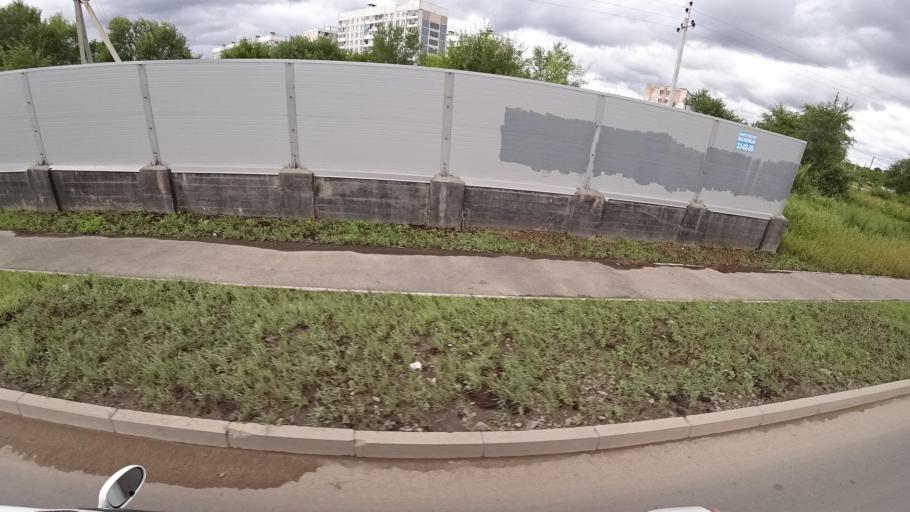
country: RU
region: Khabarovsk Krai
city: Solnechnyy
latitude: 50.5933
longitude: 137.0366
